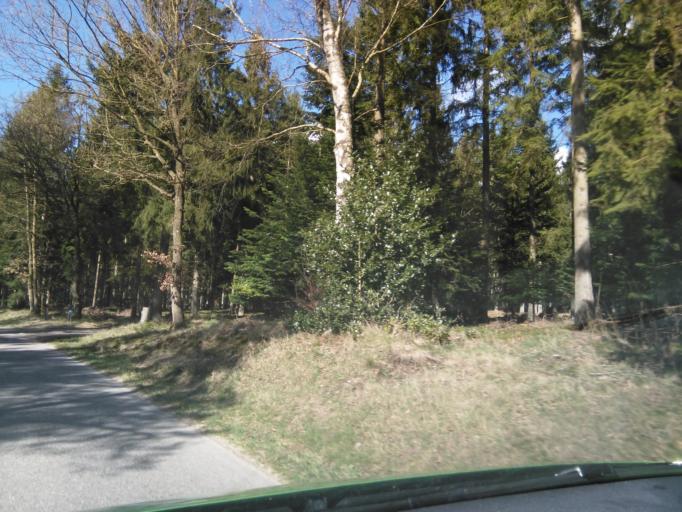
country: DK
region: Central Jutland
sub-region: Silkeborg Kommune
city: Svejbaek
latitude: 56.0690
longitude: 9.6552
